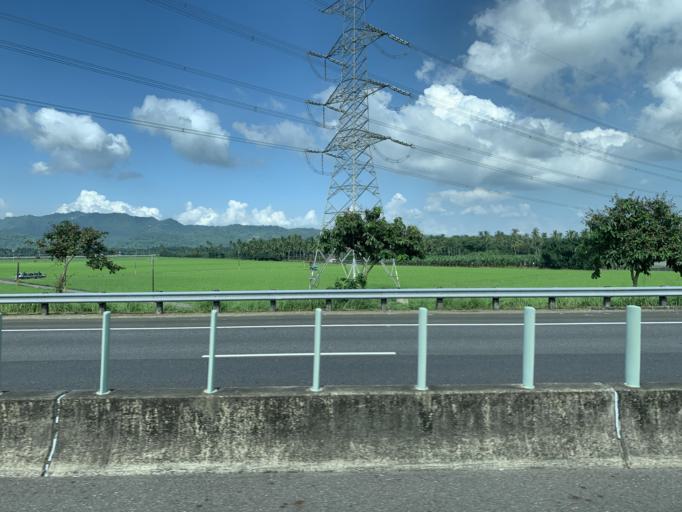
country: TW
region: Taiwan
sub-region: Pingtung
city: Pingtung
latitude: 22.8318
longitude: 120.4914
